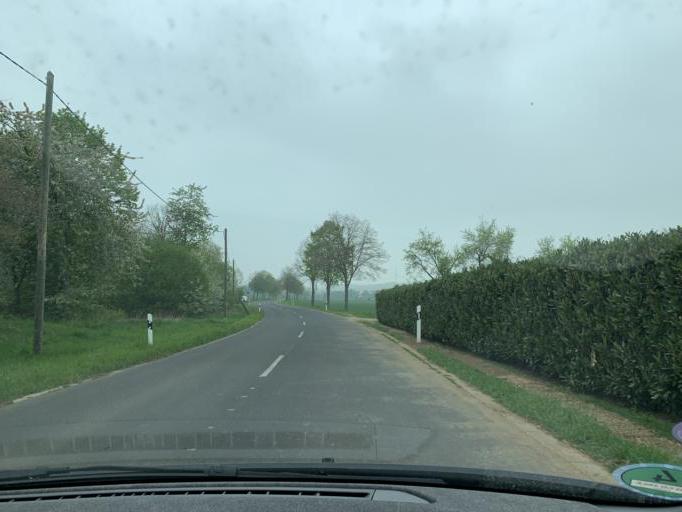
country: DE
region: North Rhine-Westphalia
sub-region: Regierungsbezirk Koln
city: Vettweiss
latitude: 50.6850
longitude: 6.5685
